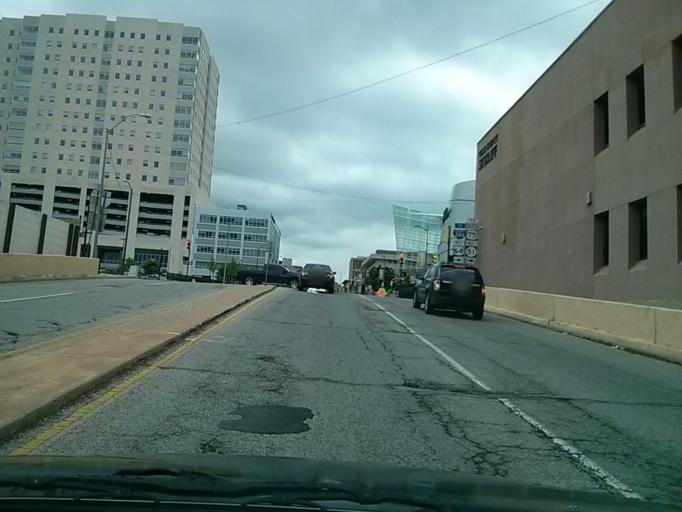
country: US
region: Oklahoma
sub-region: Tulsa County
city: Tulsa
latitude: 36.1545
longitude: -95.9959
